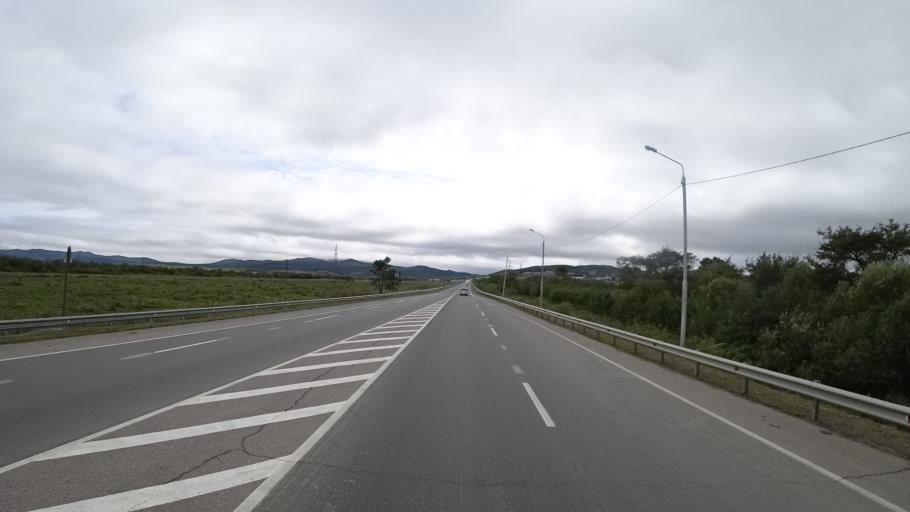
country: RU
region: Primorskiy
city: Monastyrishche
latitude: 44.1839
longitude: 132.4415
